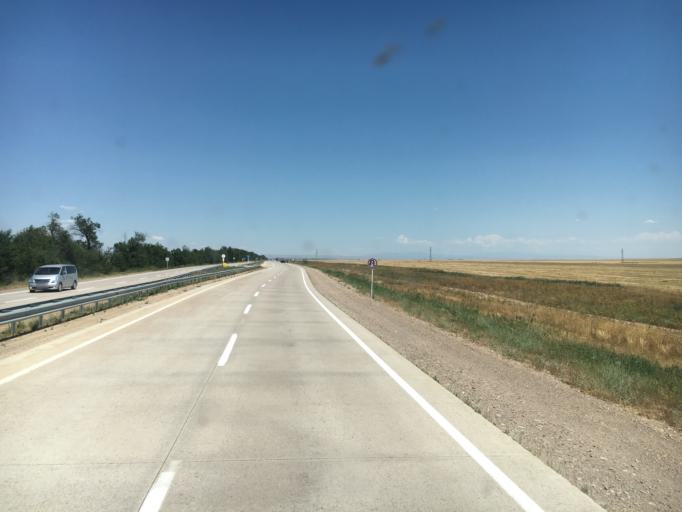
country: KG
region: Chuy
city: Belovodskoye
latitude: 43.2110
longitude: 74.1126
